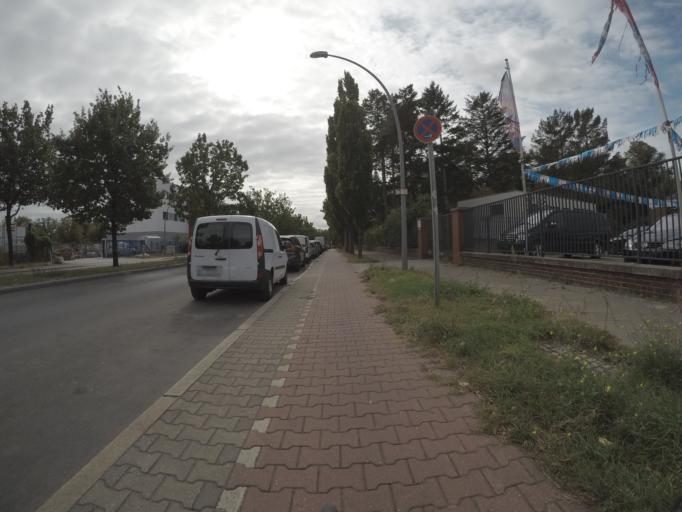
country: DE
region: Berlin
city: Tempelhof Bezirk
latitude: 52.4546
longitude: 13.4092
